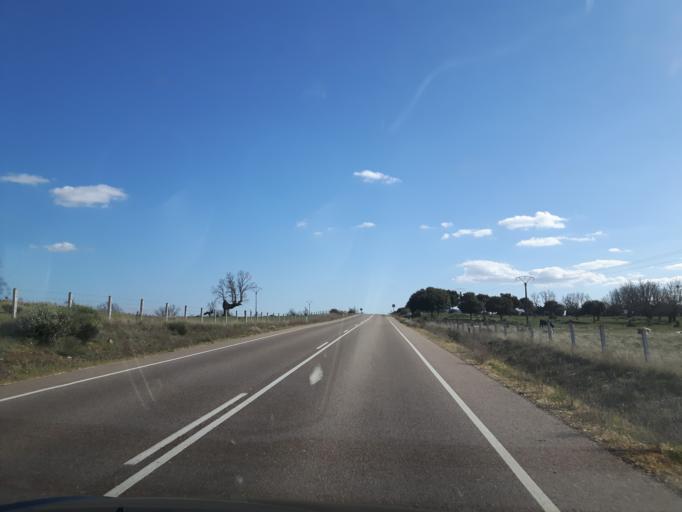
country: ES
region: Castille and Leon
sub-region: Provincia de Salamanca
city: Herguijuela del Campo
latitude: 40.6360
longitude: -5.9042
